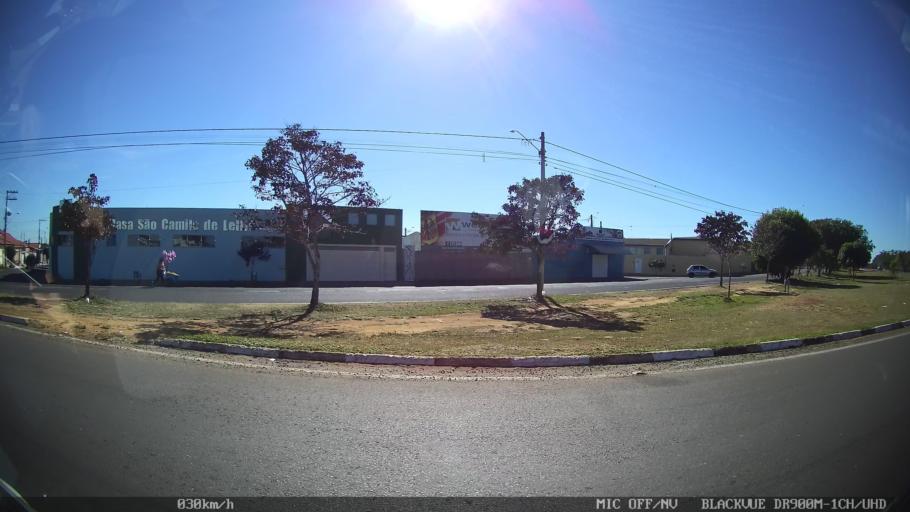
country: BR
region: Sao Paulo
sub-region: Franca
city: Franca
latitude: -20.5400
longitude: -47.3596
